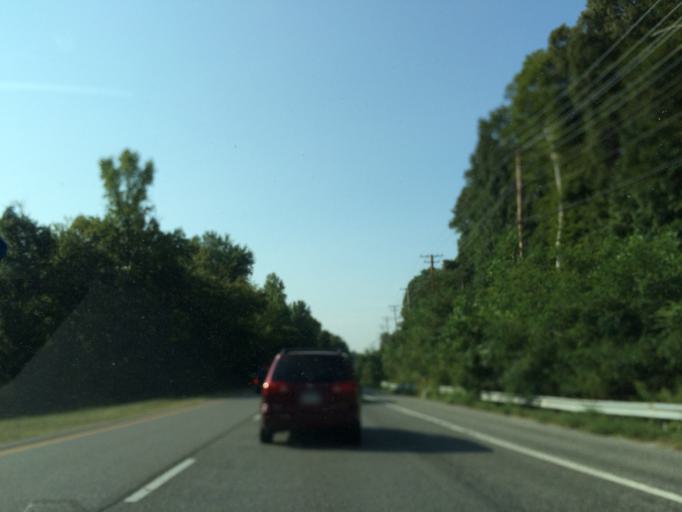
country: US
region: Maryland
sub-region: Prince George's County
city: Bowie
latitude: 38.9291
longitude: -76.7172
